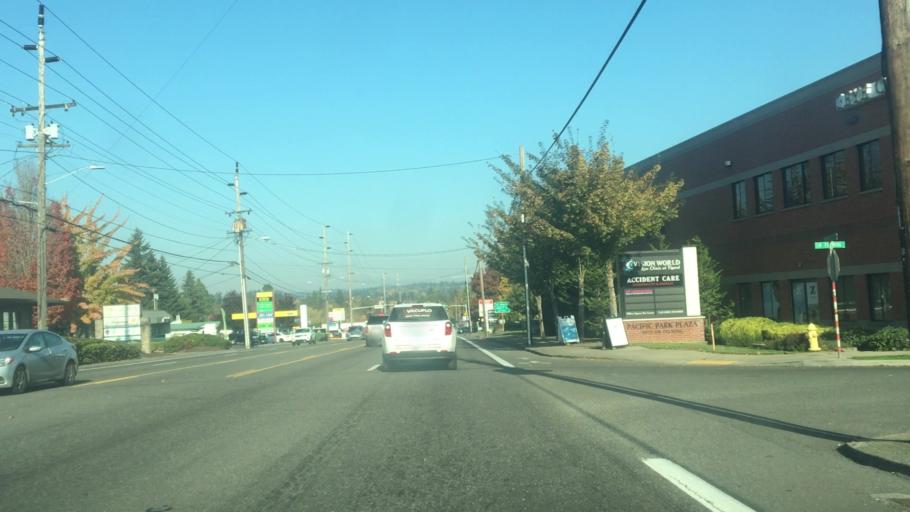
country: US
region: Oregon
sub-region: Washington County
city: Tigard
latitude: 45.4256
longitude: -122.7801
